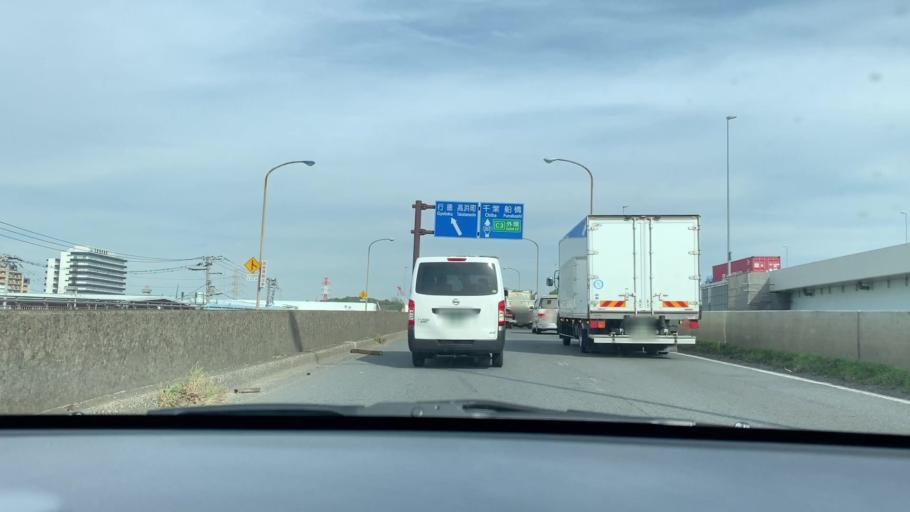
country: JP
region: Tokyo
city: Urayasu
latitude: 35.6748
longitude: 139.9296
